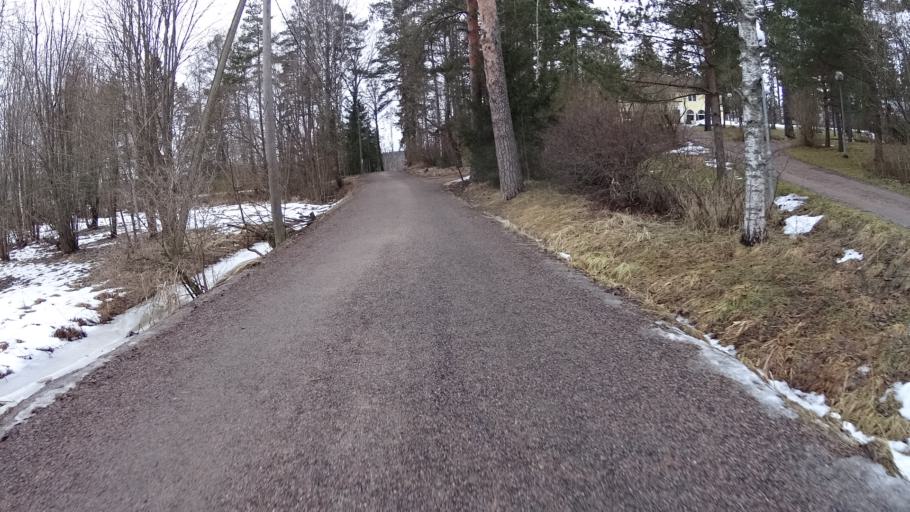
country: FI
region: Uusimaa
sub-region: Helsinki
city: Kilo
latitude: 60.2361
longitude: 24.7876
